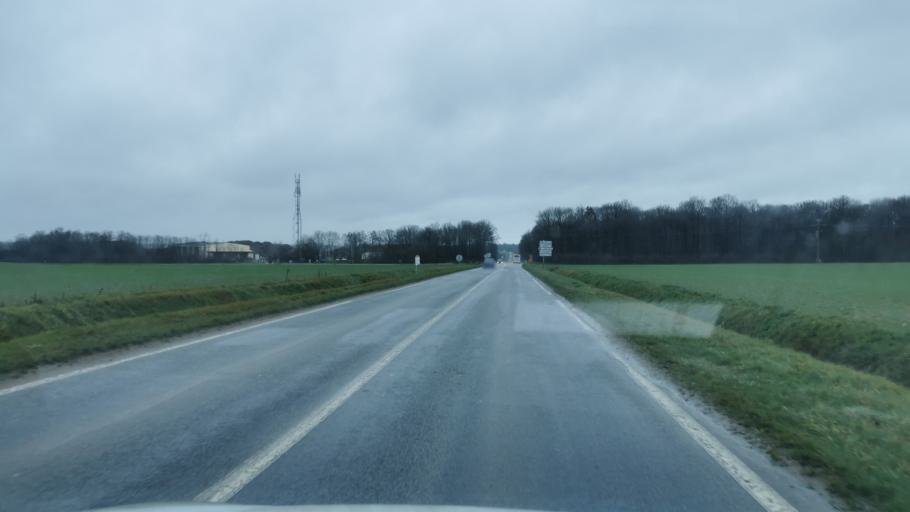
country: FR
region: Haute-Normandie
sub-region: Departement de l'Eure
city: Normanville
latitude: 49.0889
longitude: 1.1778
